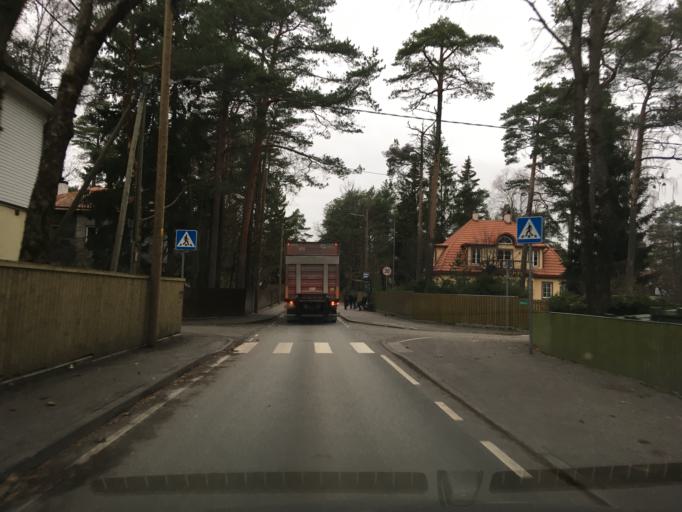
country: EE
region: Harju
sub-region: Saue vald
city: Laagri
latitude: 59.3795
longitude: 24.6752
